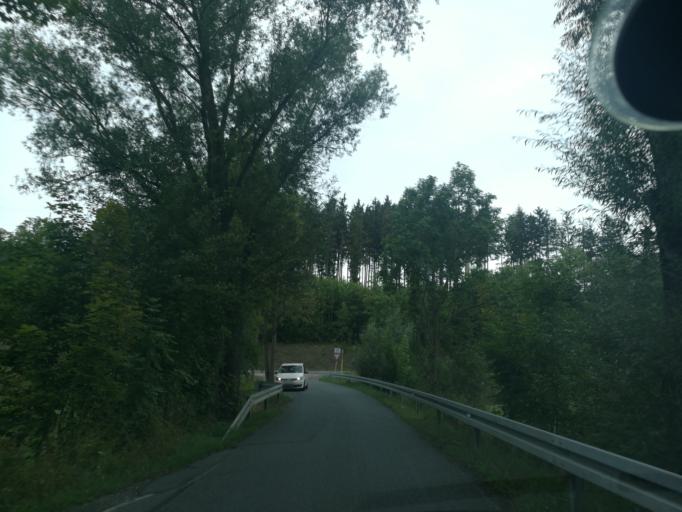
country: DE
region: Bavaria
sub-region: Upper Franconia
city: Dohlau
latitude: 50.2954
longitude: 11.9464
